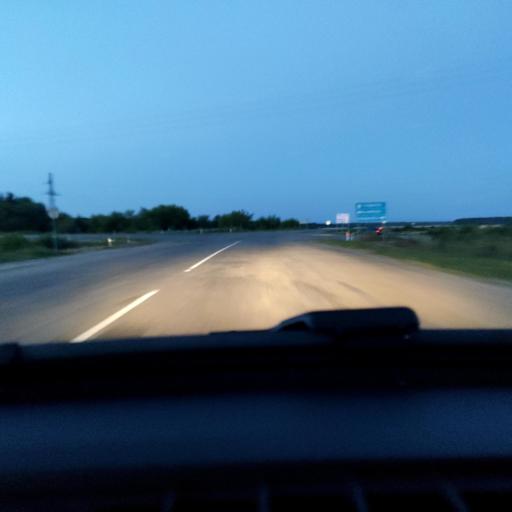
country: RU
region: Lipetsk
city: Zadonsk
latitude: 52.2994
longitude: 38.8004
